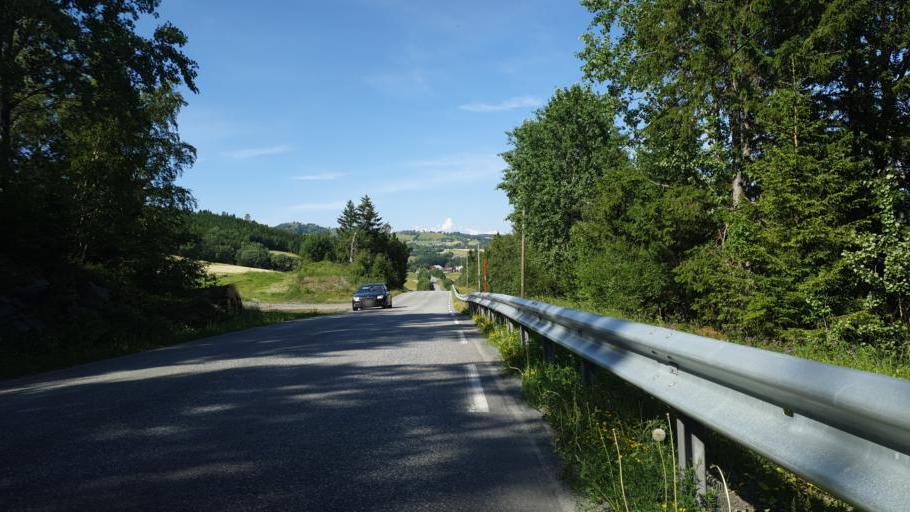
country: NO
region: Nord-Trondelag
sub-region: Leksvik
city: Leksvik
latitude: 63.6564
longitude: 10.6087
